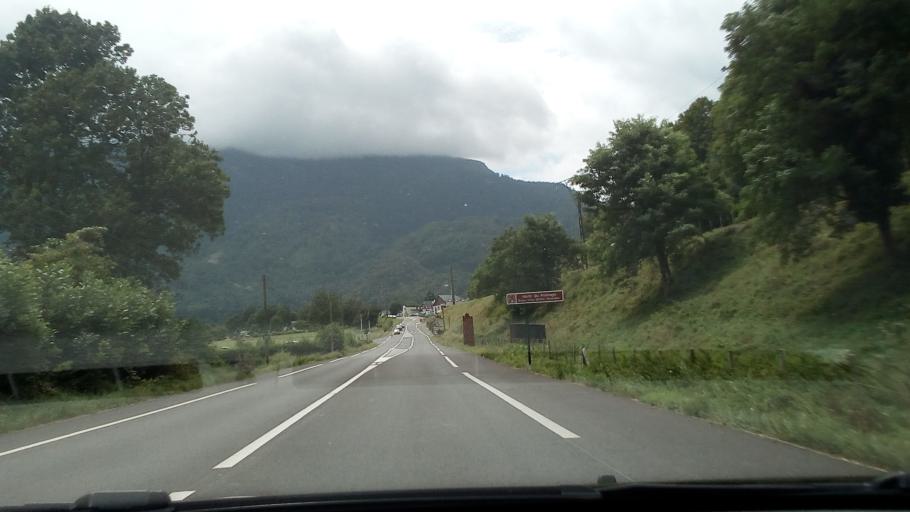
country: FR
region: Aquitaine
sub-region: Departement des Pyrenees-Atlantiques
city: Laruns
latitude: 42.9960
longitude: -0.4220
